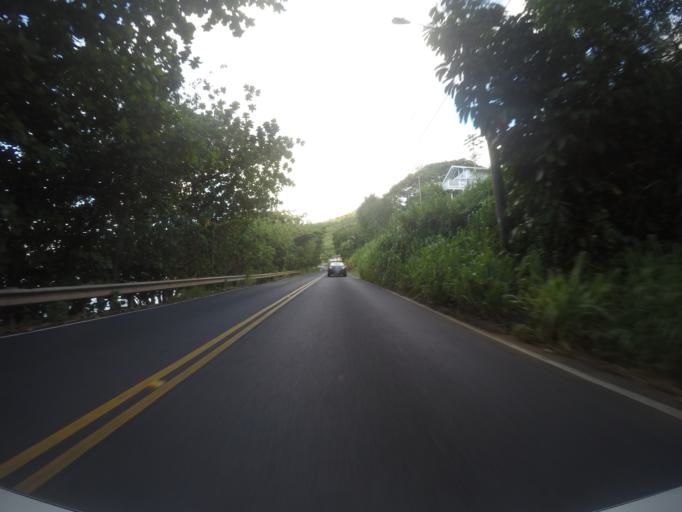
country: US
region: Hawaii
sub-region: Honolulu County
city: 'Ahuimanu
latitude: 21.4554
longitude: -157.8269
